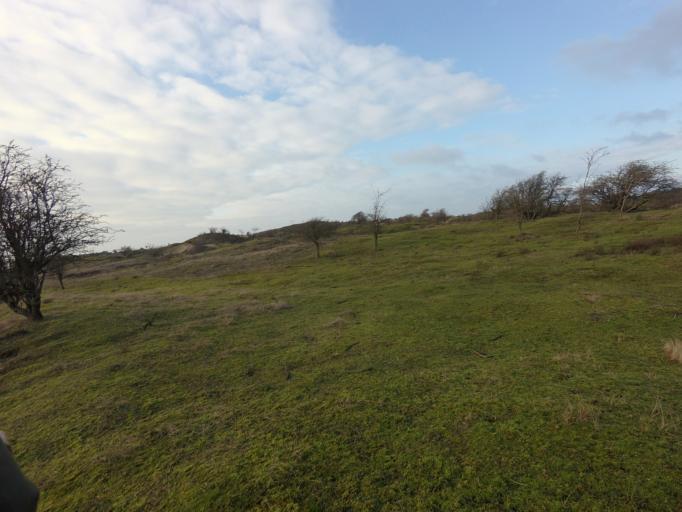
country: NL
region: North Holland
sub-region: Gemeente Zandvoort
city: Zandvoort
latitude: 52.3201
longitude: 4.5203
